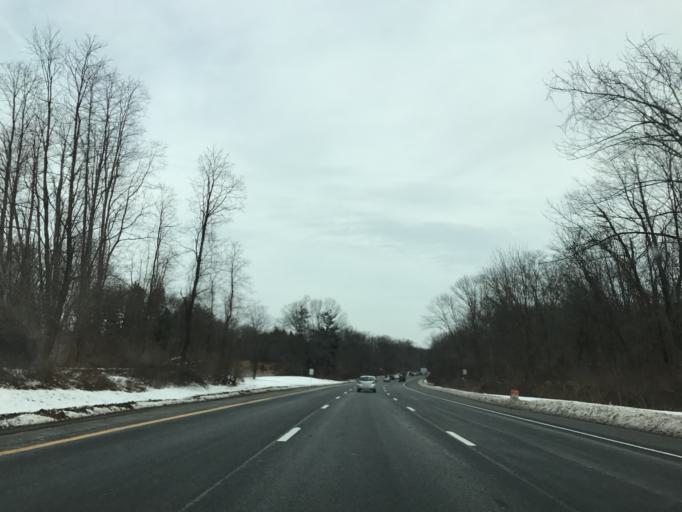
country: US
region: New Jersey
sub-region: Morris County
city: Morristown
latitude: 40.7613
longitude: -74.5158
